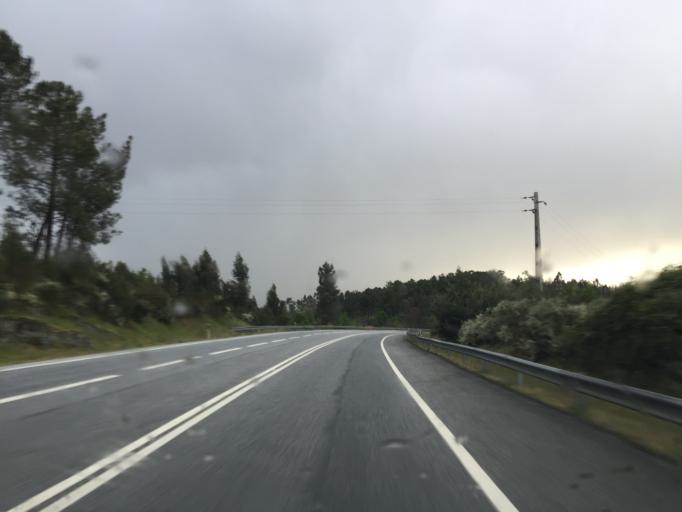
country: PT
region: Viseu
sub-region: Viseu
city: Viseu
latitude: 40.6084
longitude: -7.9628
